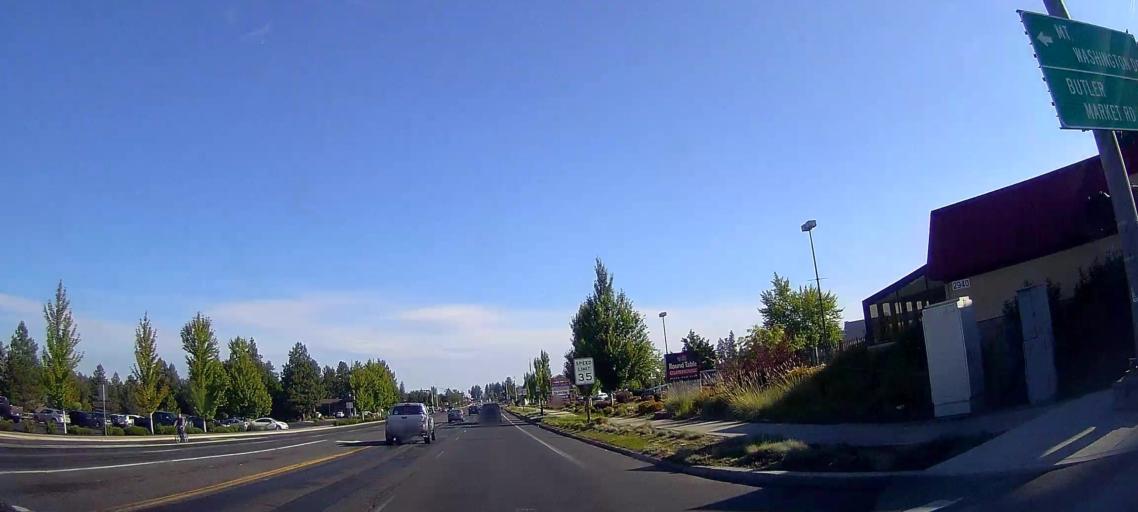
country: US
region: Oregon
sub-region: Deschutes County
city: Bend
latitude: 44.0795
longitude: -121.3048
